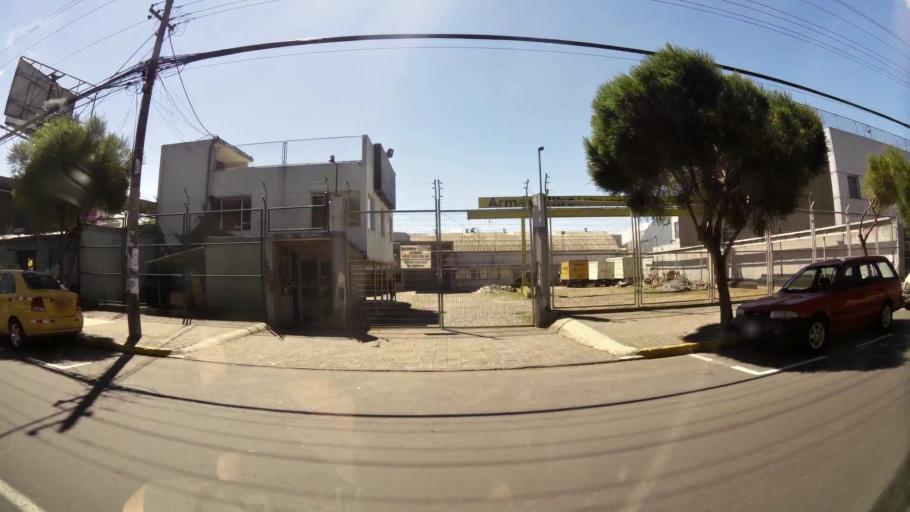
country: EC
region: Pichincha
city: Quito
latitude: -0.1574
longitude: -78.4882
